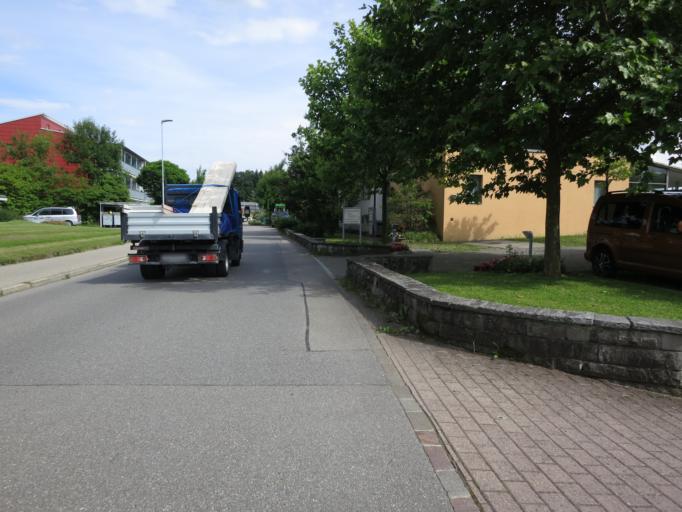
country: CH
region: Zurich
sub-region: Bezirk Hinwil
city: Wolfhausen
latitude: 47.2545
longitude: 8.8029
